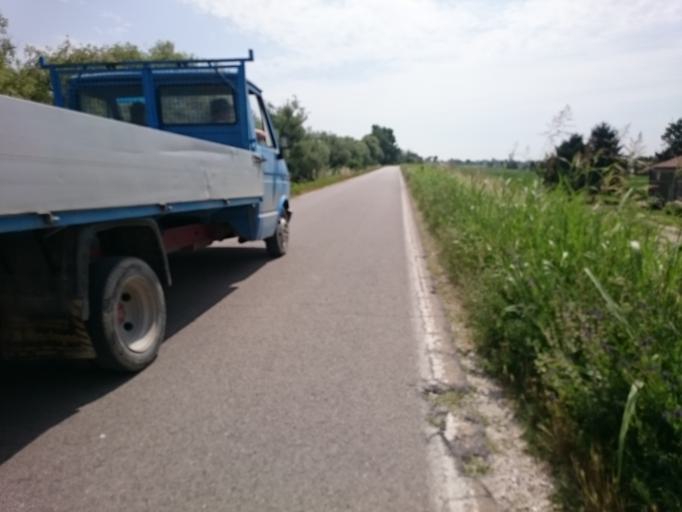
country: IT
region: Veneto
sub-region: Provincia di Padova
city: Pontelongo
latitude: 45.2432
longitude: 12.0447
